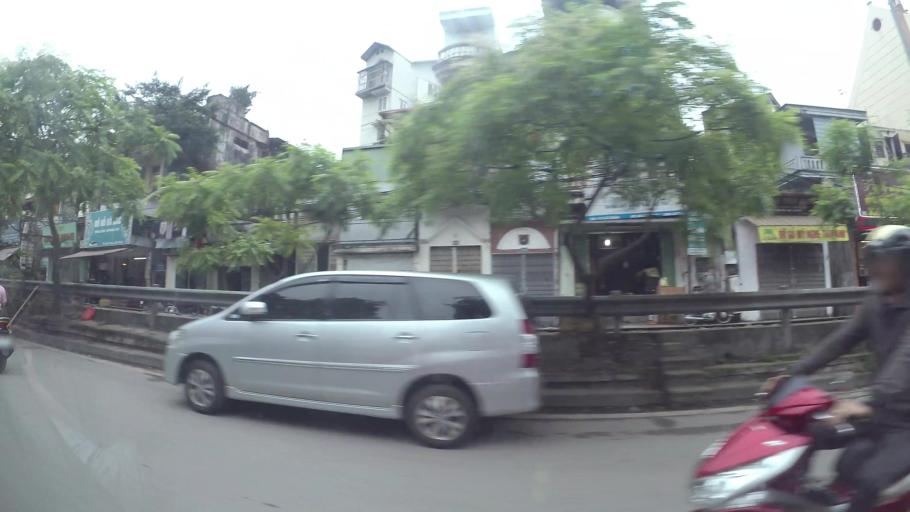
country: VN
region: Ha Noi
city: Hai BaTrung
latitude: 21.0094
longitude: 105.8411
